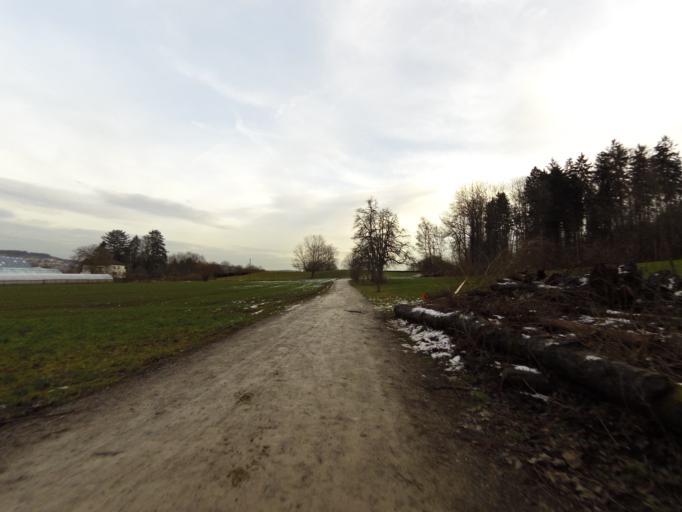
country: CH
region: Zurich
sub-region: Bezirk Zuerich
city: Zuerich (Kreis 9)
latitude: 47.3862
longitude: 8.4667
